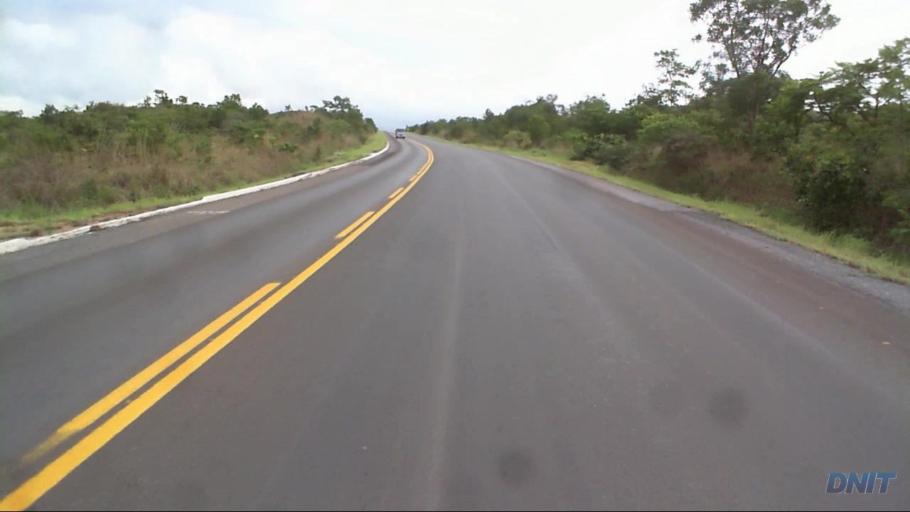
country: BR
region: Goias
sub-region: Padre Bernardo
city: Padre Bernardo
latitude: -15.2124
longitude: -48.5731
